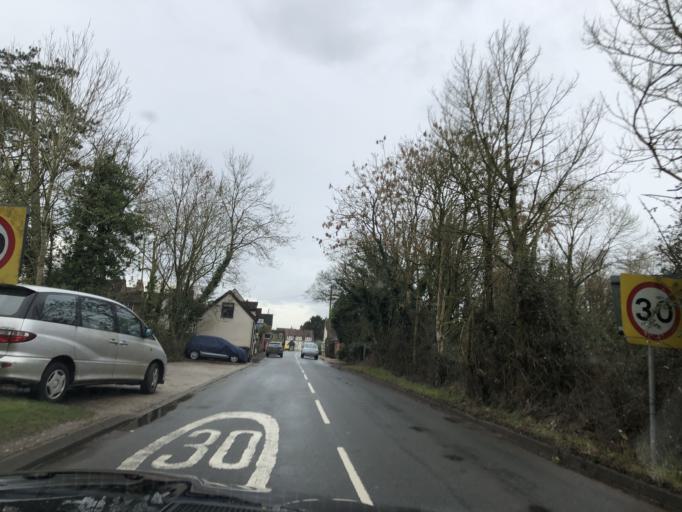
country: GB
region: England
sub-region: Warwickshire
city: Henley in Arden
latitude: 52.2844
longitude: -1.7139
